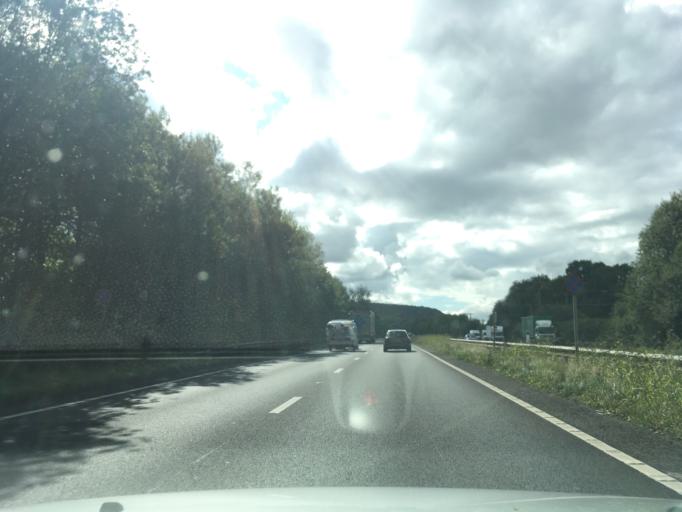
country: GB
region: England
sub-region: Hampshire
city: Petersfield
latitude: 50.9953
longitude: -0.9528
